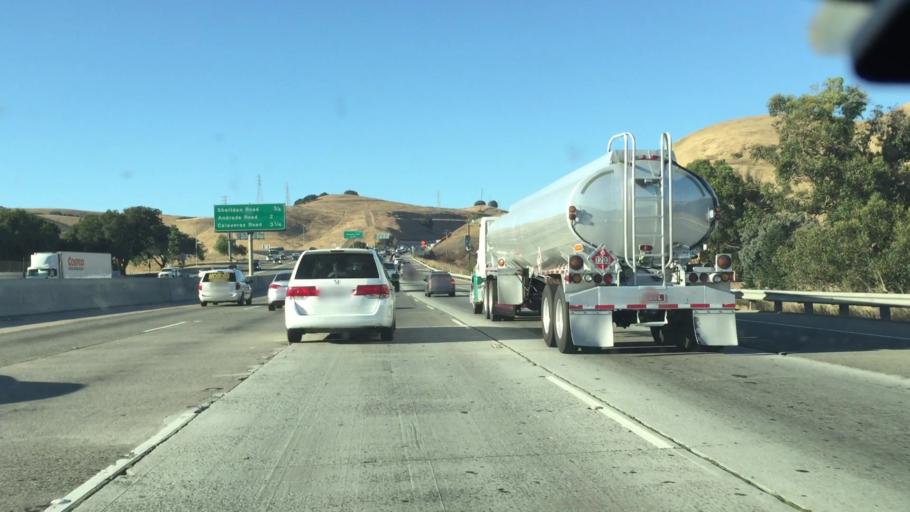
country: US
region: California
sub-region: Alameda County
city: Fremont
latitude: 37.5518
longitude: -121.9179
